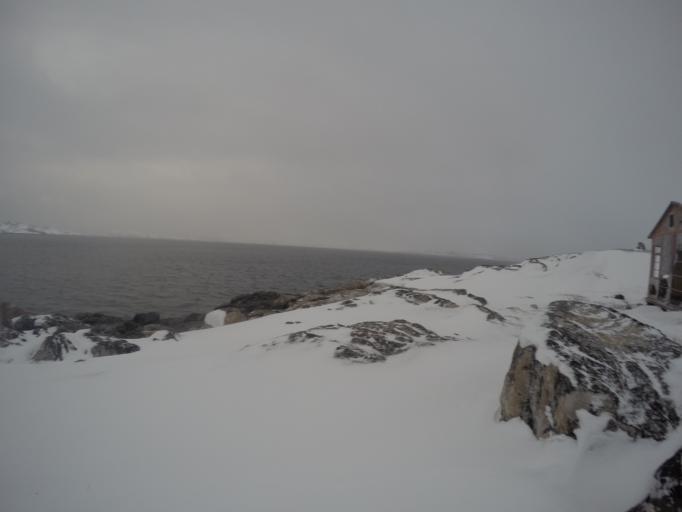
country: GL
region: Sermersooq
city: Nuuk
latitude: 64.1430
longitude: -51.6800
